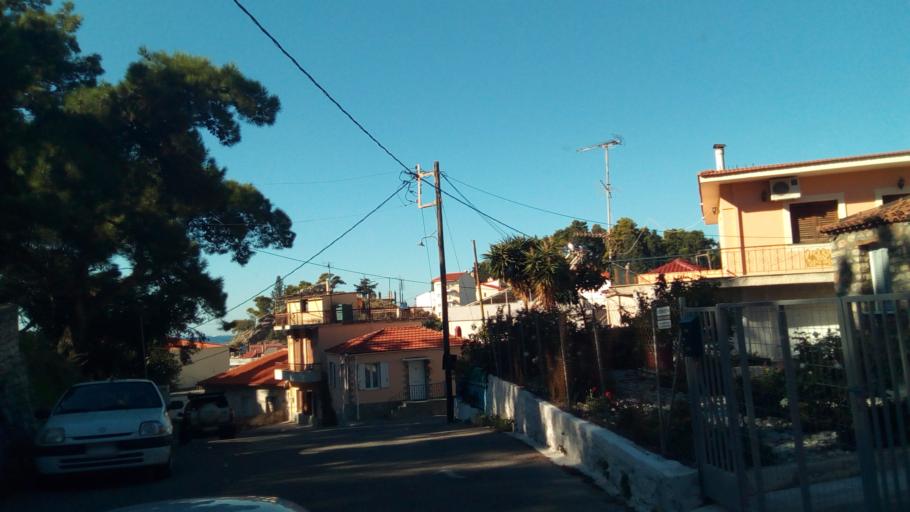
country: GR
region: West Greece
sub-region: Nomos Aitolias kai Akarnanias
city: Nafpaktos
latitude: 38.3958
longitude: 21.8402
